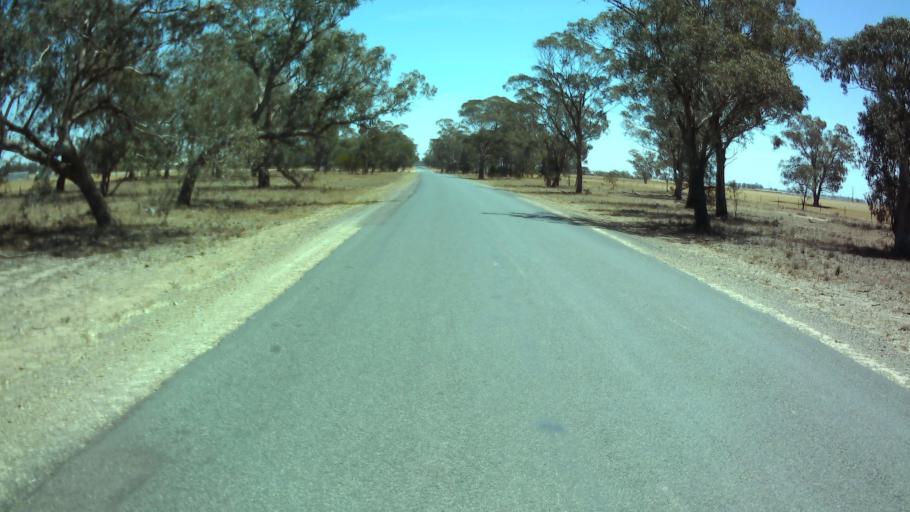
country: AU
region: New South Wales
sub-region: Weddin
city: Grenfell
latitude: -34.0131
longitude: 147.8193
